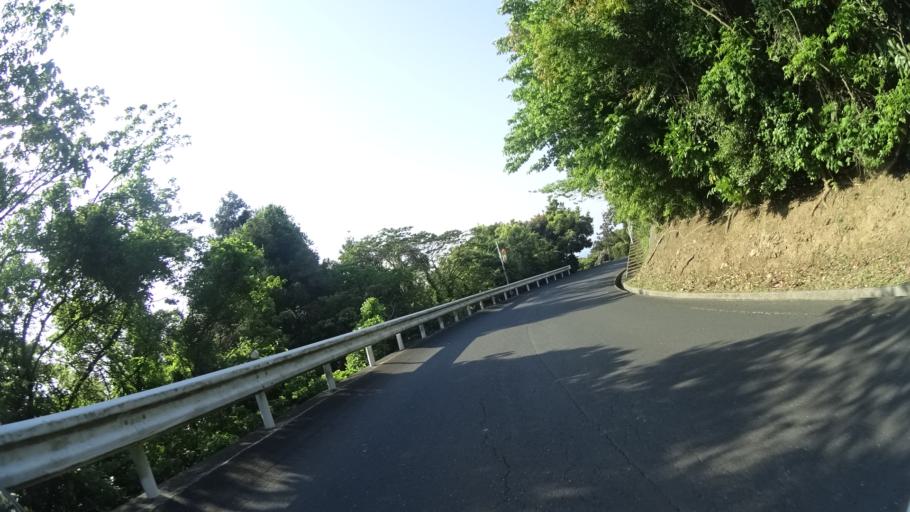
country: JP
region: Ehime
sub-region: Nishiuwa-gun
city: Ikata-cho
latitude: 33.3719
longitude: 132.0574
